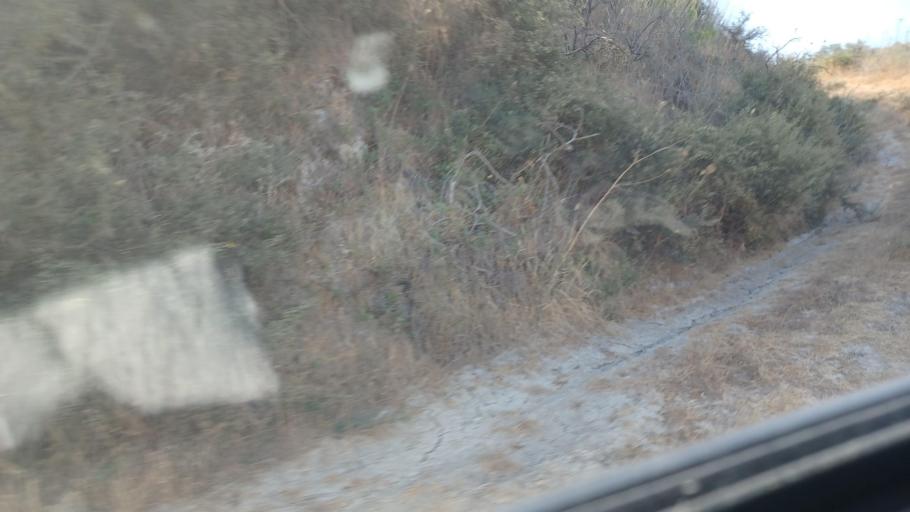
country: CY
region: Pafos
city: Tala
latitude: 34.8911
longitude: 32.4644
